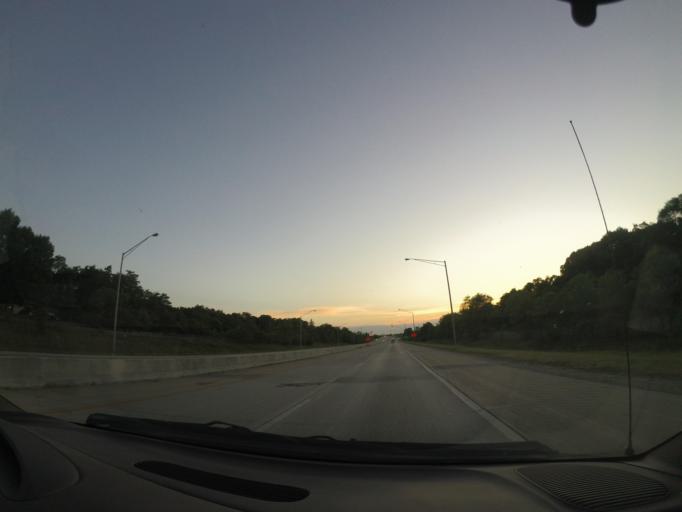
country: US
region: Indiana
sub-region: Elkhart County
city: Dunlap
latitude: 41.6671
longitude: -85.8741
